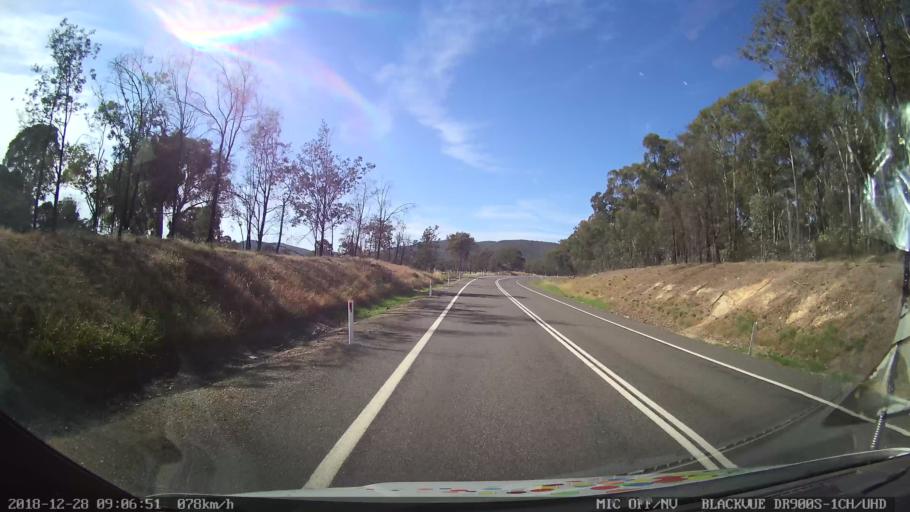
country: AU
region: New South Wales
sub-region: Upper Lachlan Shire
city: Crookwell
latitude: -34.2005
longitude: 149.3461
